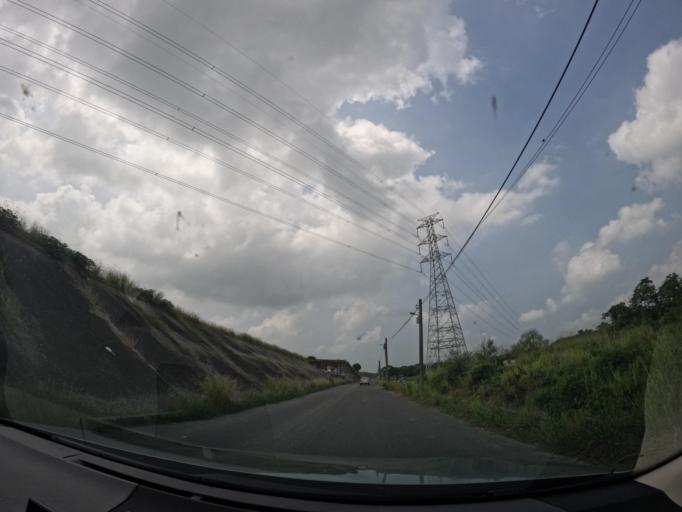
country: TW
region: Taiwan
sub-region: Chiayi
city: Taibao
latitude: 23.5968
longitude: 120.3537
